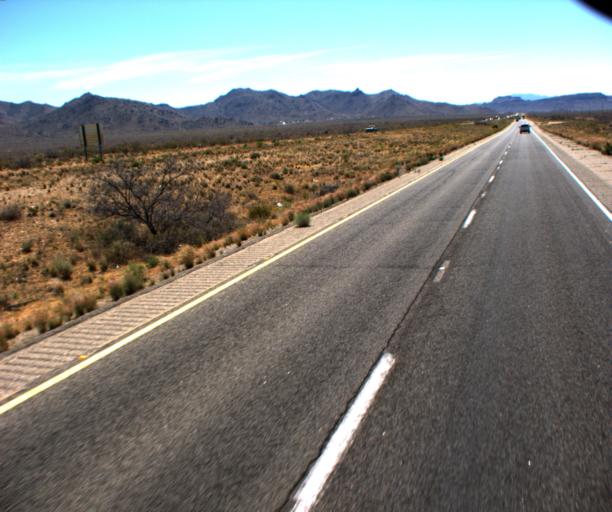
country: US
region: Arizona
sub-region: Mohave County
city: Golden Valley
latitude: 35.2864
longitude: -114.1796
